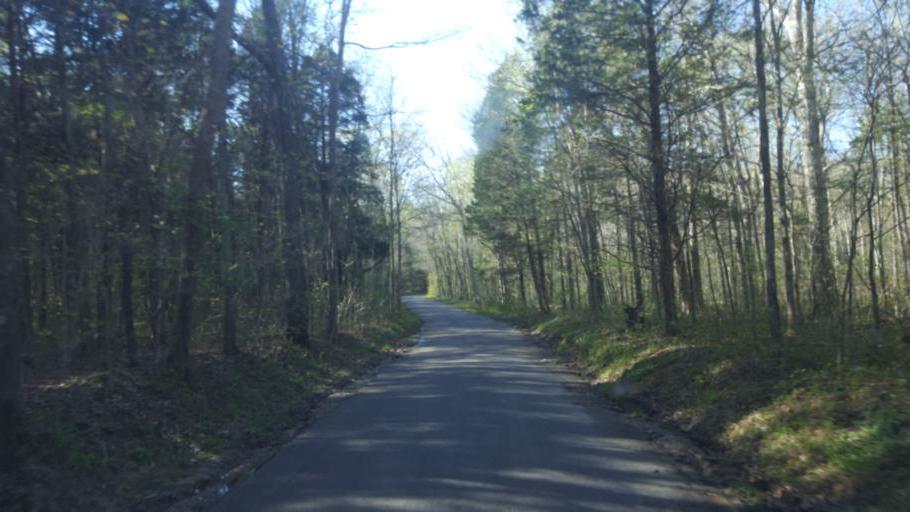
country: US
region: Kentucky
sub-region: Barren County
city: Cave City
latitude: 37.1868
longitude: -86.0482
